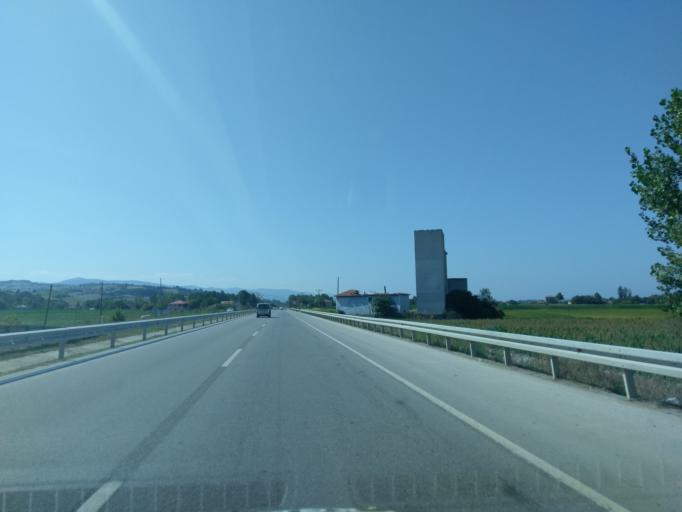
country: TR
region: Samsun
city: Alacam
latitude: 41.6094
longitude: 35.6579
